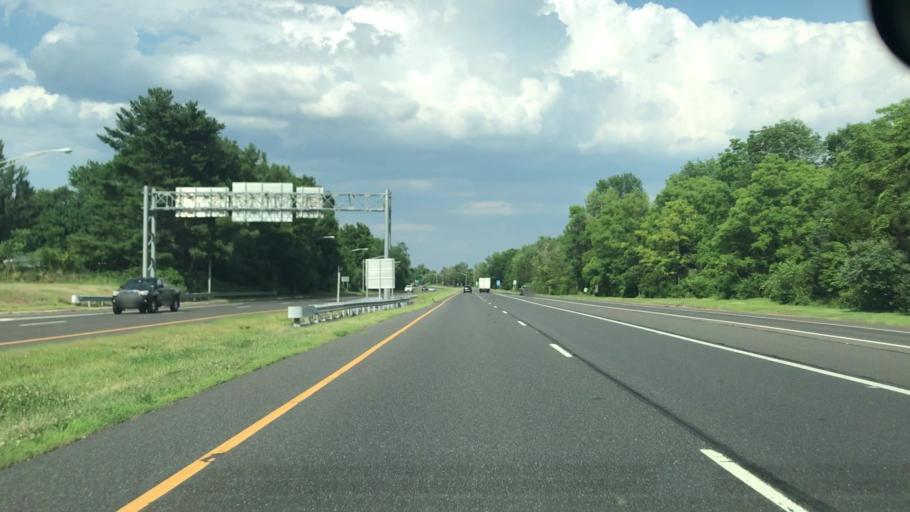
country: US
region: New Jersey
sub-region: Hunterdon County
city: Lambertville
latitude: 40.4192
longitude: -74.8735
